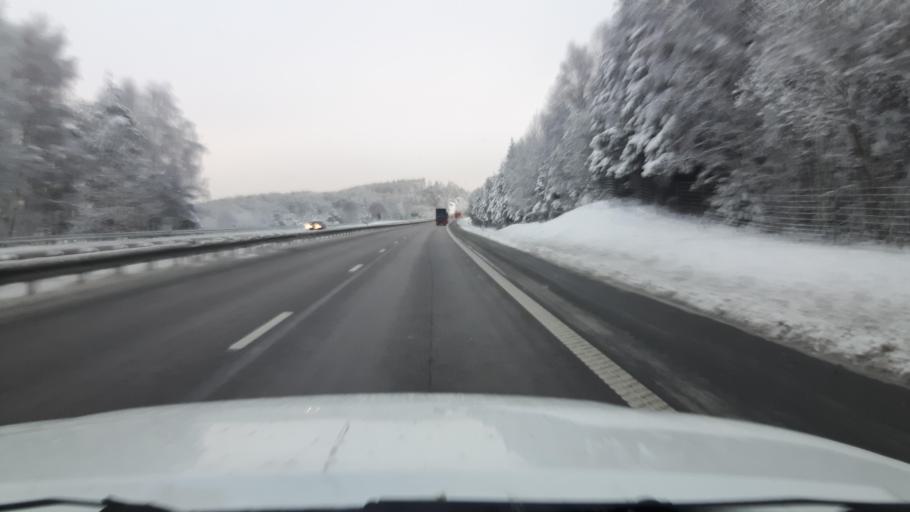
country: SE
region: Halland
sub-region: Kungsbacka Kommun
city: Frillesas
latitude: 57.3810
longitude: 12.1948
